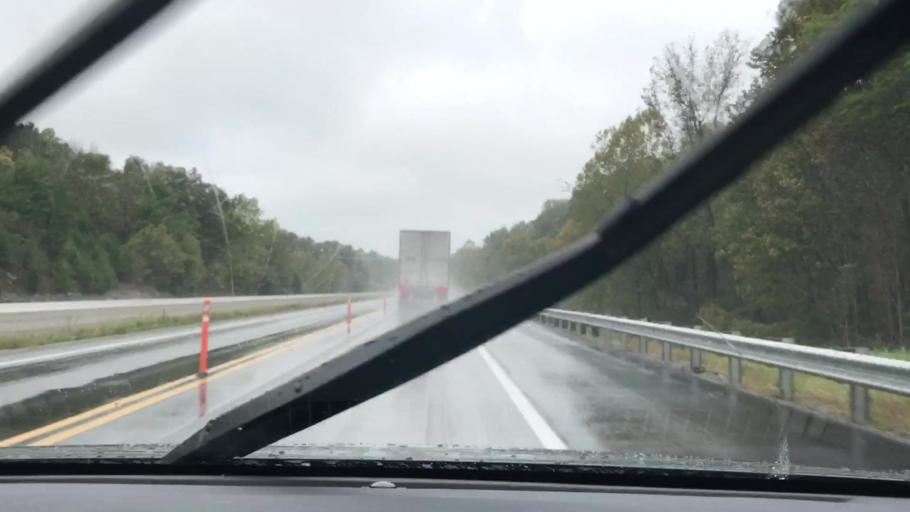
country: US
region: Kentucky
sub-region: Christian County
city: Hopkinsville
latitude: 37.0061
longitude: -87.4607
